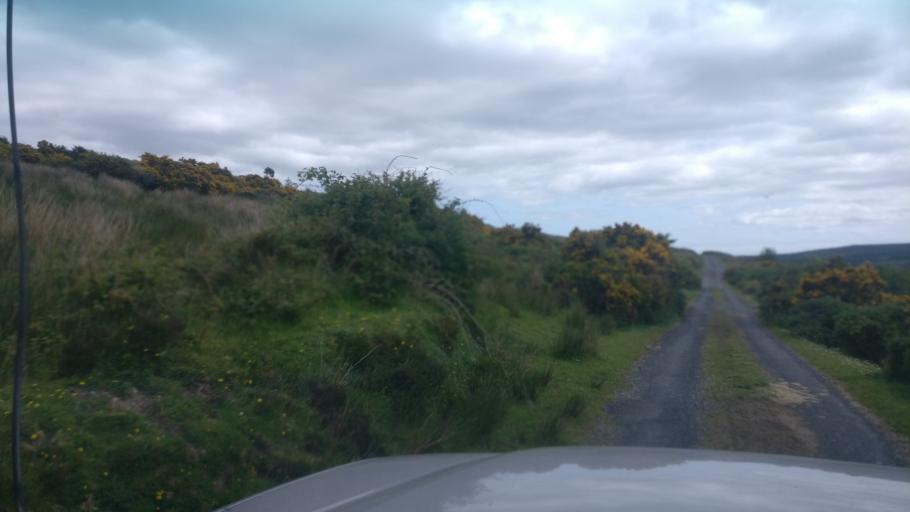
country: IE
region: Connaught
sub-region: County Galway
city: Loughrea
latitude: 53.1169
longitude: -8.6452
